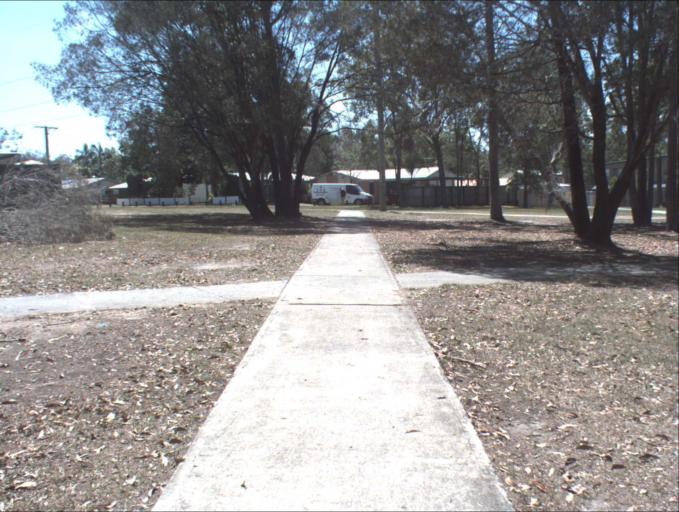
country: AU
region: Queensland
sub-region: Logan
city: Beenleigh
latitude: -27.6984
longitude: 153.2086
